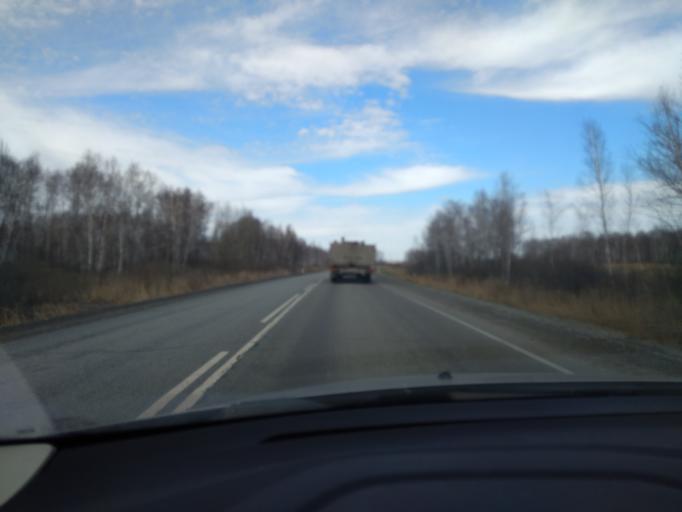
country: RU
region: Sverdlovsk
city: Pyshma
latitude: 56.9741
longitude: 63.2327
